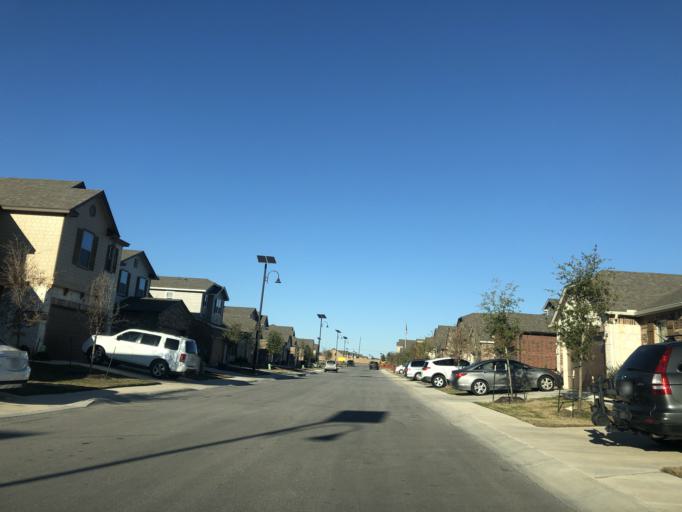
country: US
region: Texas
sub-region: Travis County
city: Windemere
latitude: 30.4721
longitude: -97.6590
